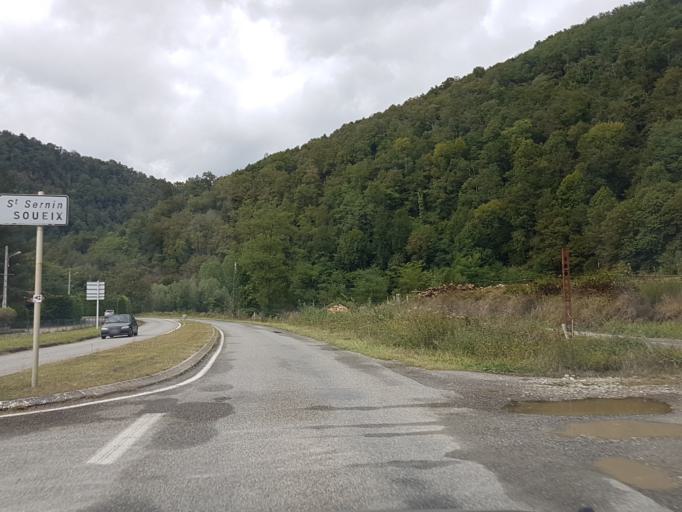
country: FR
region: Midi-Pyrenees
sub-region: Departement de l'Ariege
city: Saint-Girons
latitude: 42.8993
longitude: 1.2144
